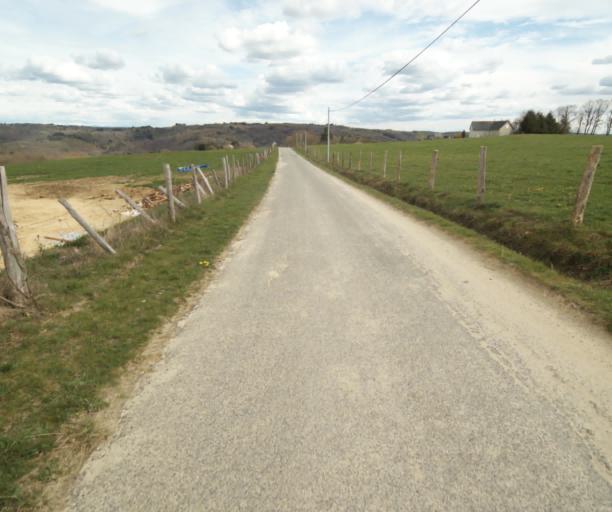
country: FR
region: Limousin
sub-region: Departement de la Correze
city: Argentat
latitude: 45.1818
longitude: 1.9424
